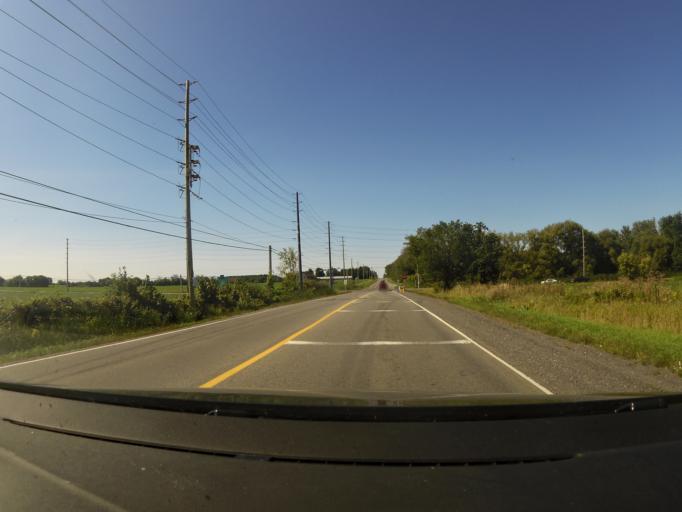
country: CA
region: Ontario
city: Bells Corners
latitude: 45.3102
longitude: -75.9453
